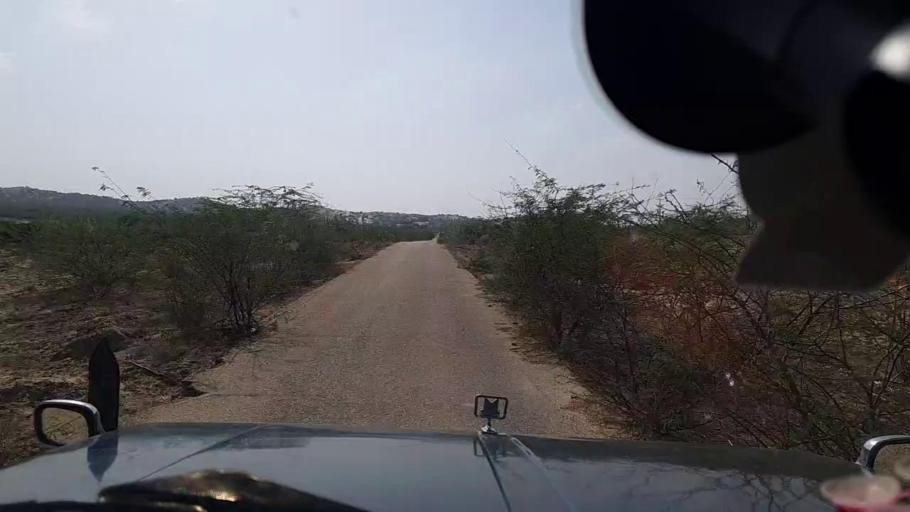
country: PK
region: Sindh
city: Diplo
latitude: 24.4187
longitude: 69.4668
